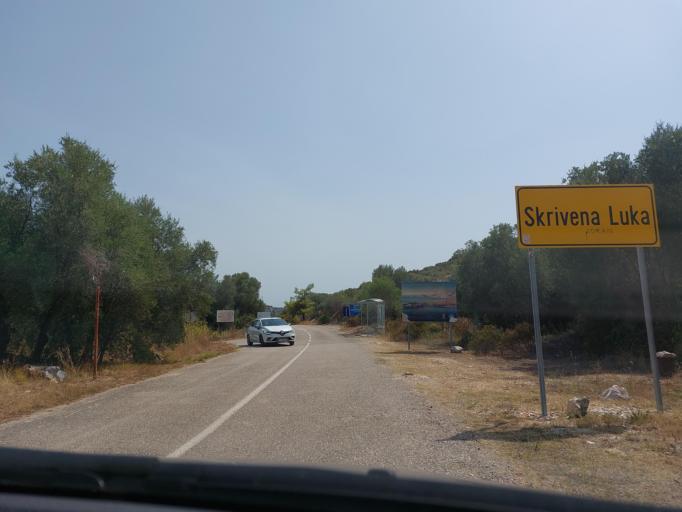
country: HR
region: Dubrovacko-Neretvanska
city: Smokvica
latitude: 42.7413
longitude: 16.8839
